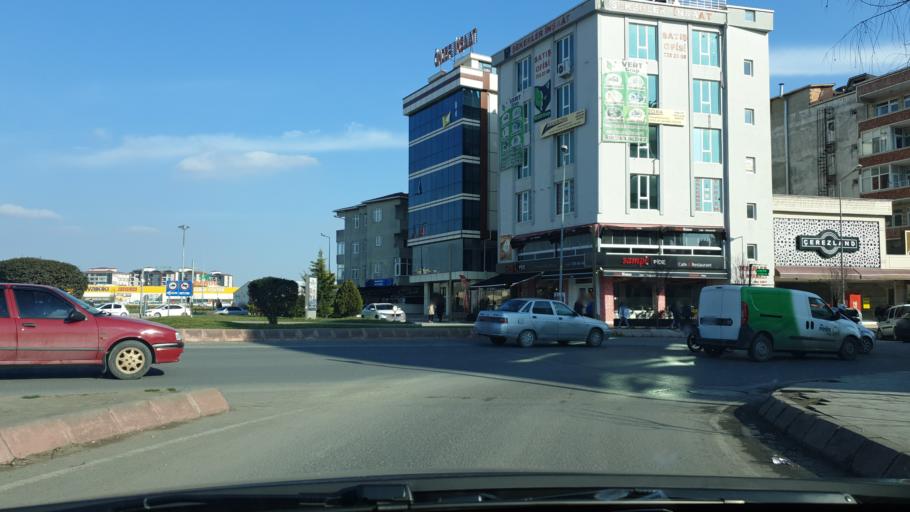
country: TR
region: Tekirdag
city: Cerkezkoey
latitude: 41.2957
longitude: 27.9972
